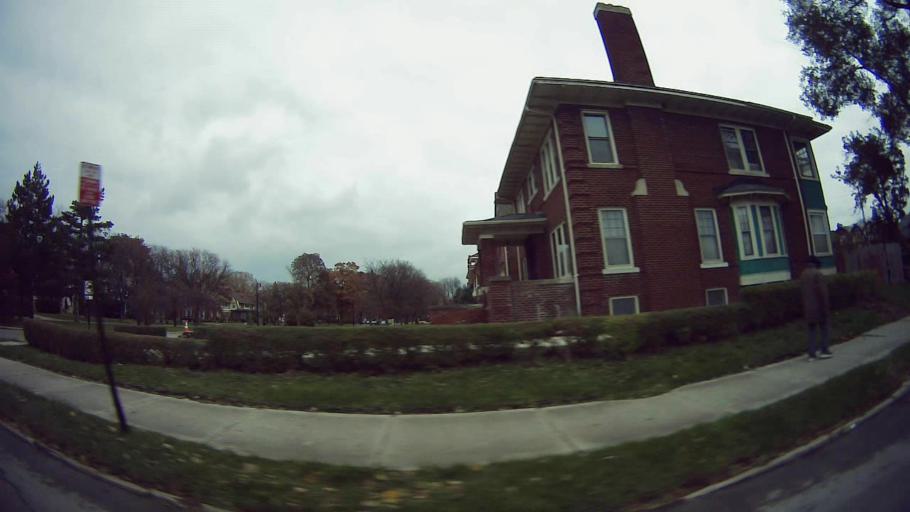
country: US
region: Michigan
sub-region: Wayne County
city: Highland Park
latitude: 42.3788
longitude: -83.1011
